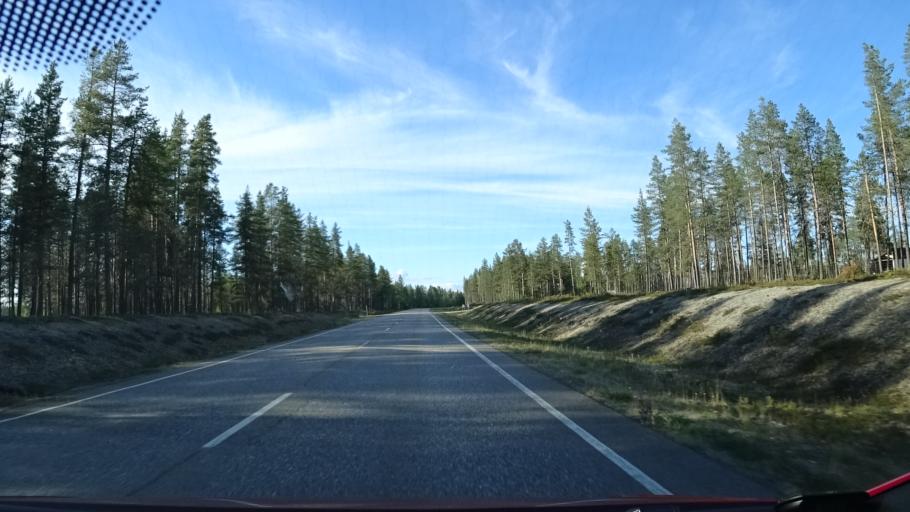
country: FI
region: Lapland
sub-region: Pohjois-Lappi
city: Sodankylae
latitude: 67.8694
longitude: 26.7317
